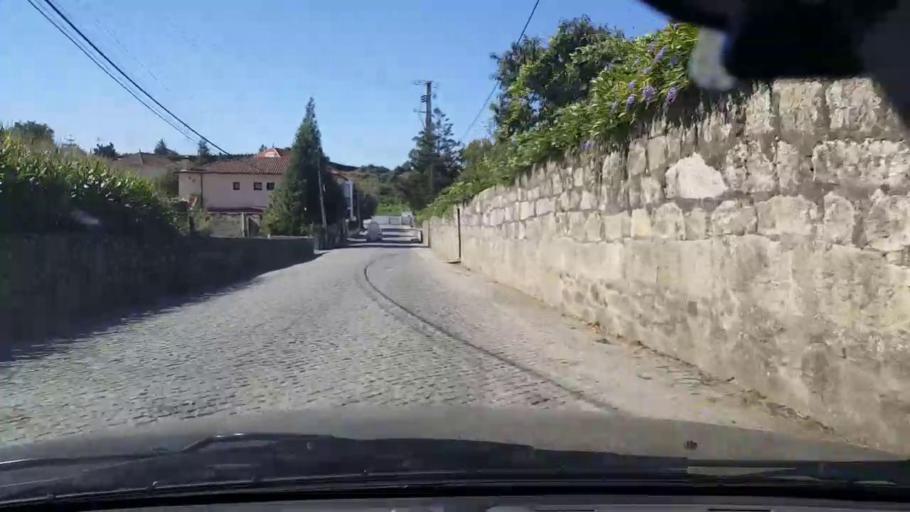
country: PT
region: Porto
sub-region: Maia
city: Gemunde
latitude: 41.2794
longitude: -8.6700
